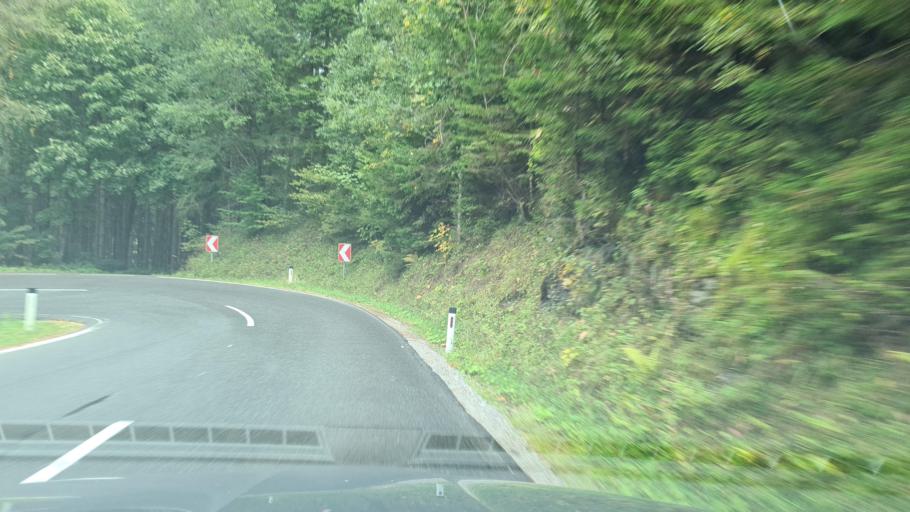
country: AT
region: Styria
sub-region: Politischer Bezirk Weiz
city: Gasen
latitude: 47.3791
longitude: 15.4905
